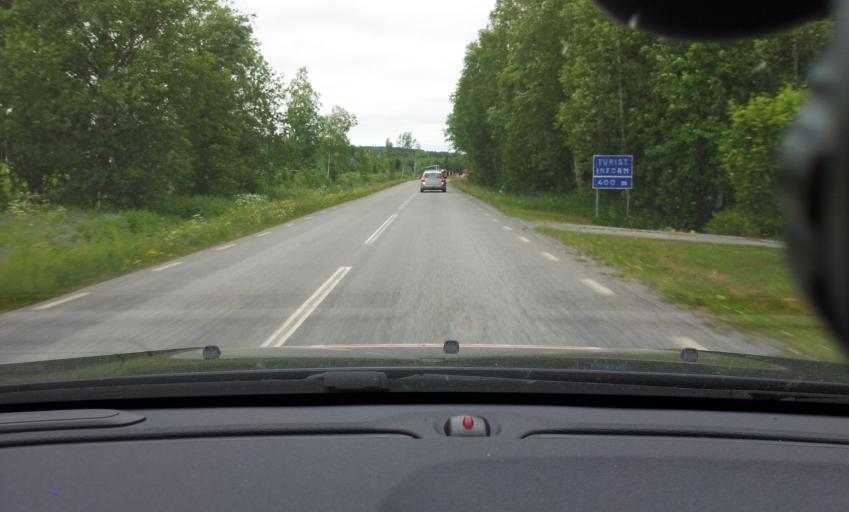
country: SE
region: Jaemtland
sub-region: Krokoms Kommun
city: Krokom
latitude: 63.1671
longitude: 14.1123
